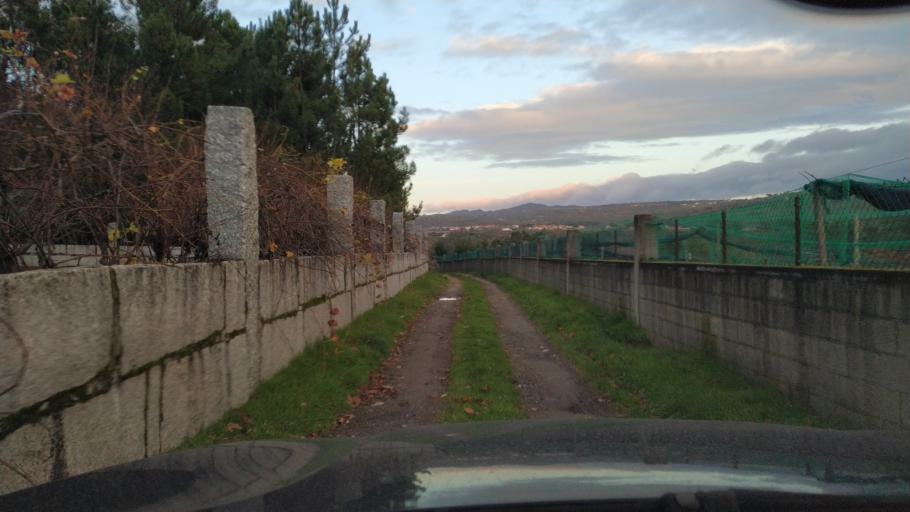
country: PT
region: Vila Real
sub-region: Vila Real
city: Vila Real
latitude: 41.3474
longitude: -7.7200
